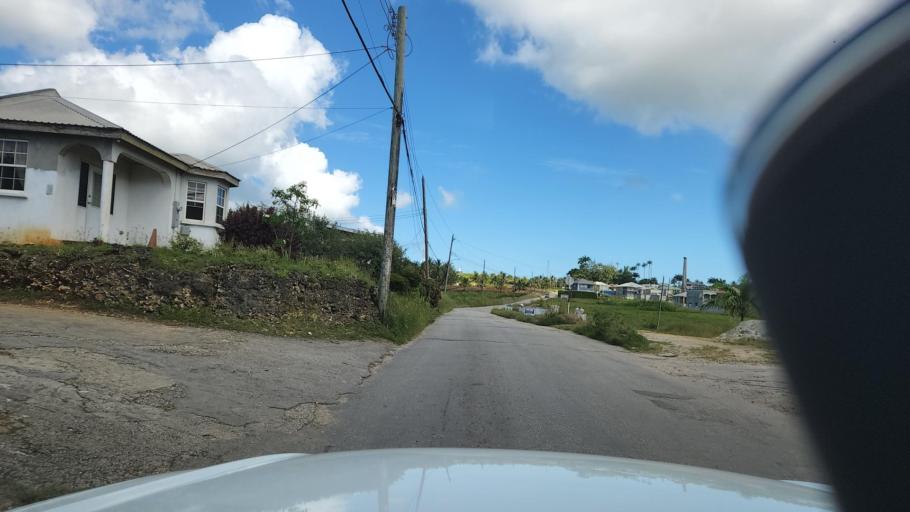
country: BB
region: Saint Thomas
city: Welchman Hall
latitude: 13.1848
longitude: -59.5683
